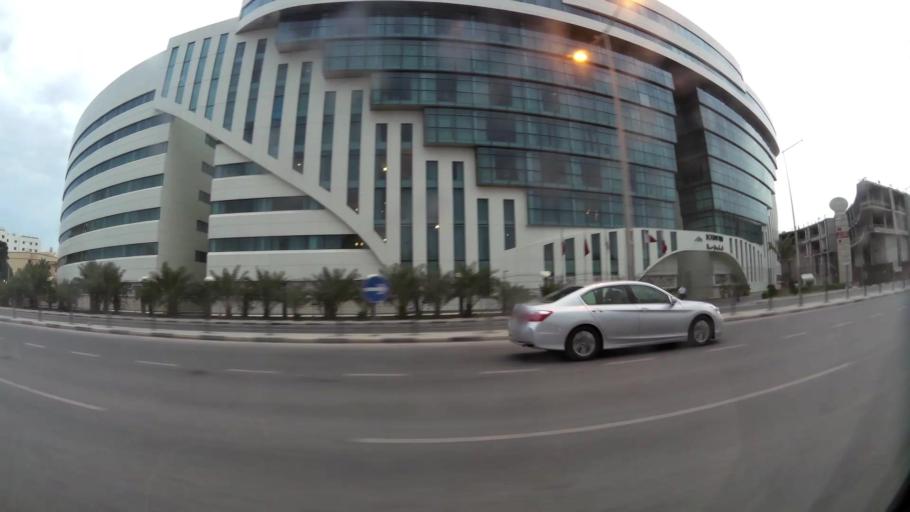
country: QA
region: Baladiyat ad Dawhah
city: Doha
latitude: 25.2647
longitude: 51.5249
